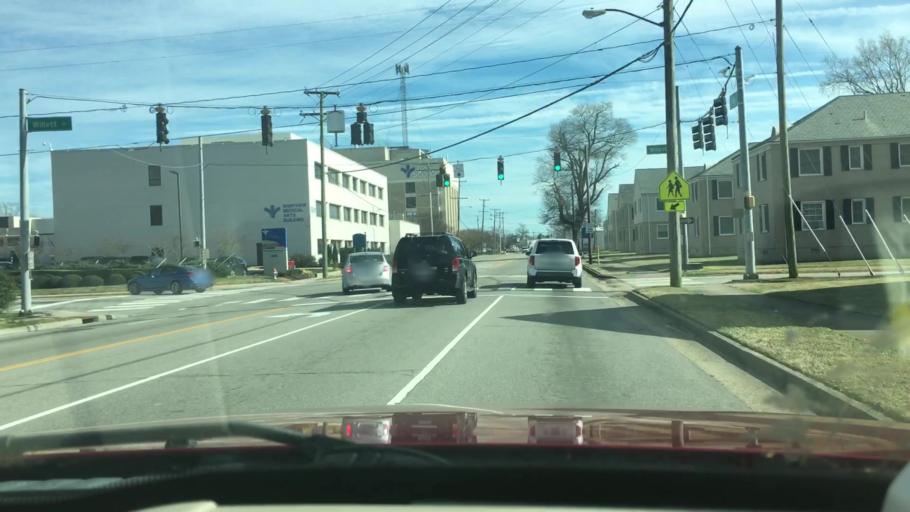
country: US
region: Virginia
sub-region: City of Portsmouth
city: Portsmouth Heights
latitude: 36.8374
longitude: -76.3503
